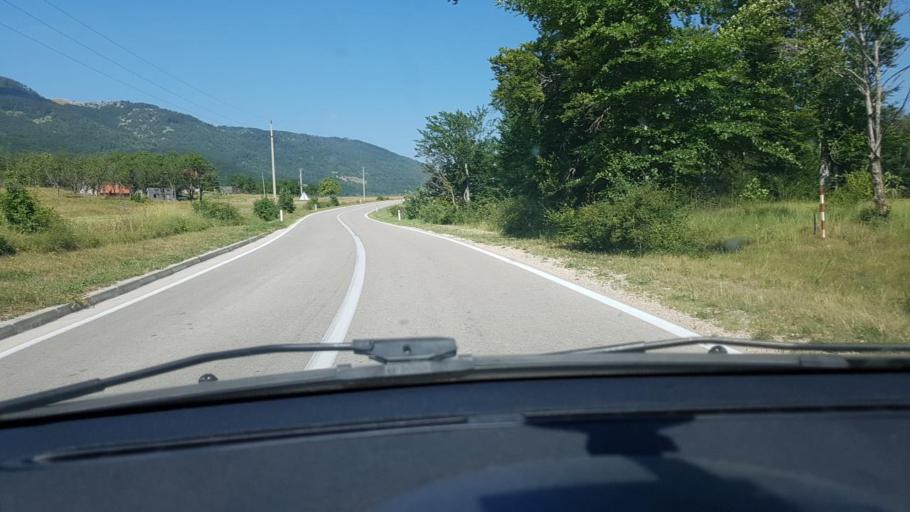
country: BA
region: Federation of Bosnia and Herzegovina
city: Bosansko Grahovo
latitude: 44.1100
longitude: 16.5470
